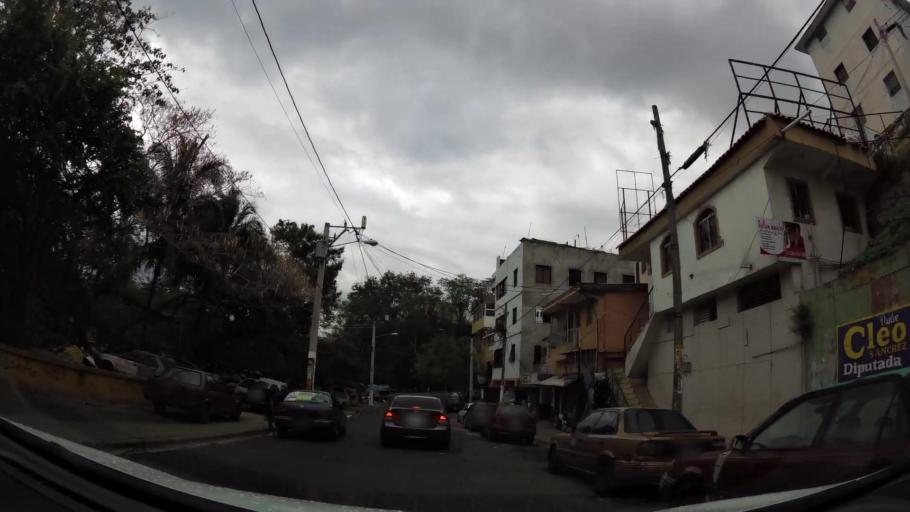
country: DO
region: Nacional
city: La Agustina
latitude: 18.4970
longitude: -69.9304
